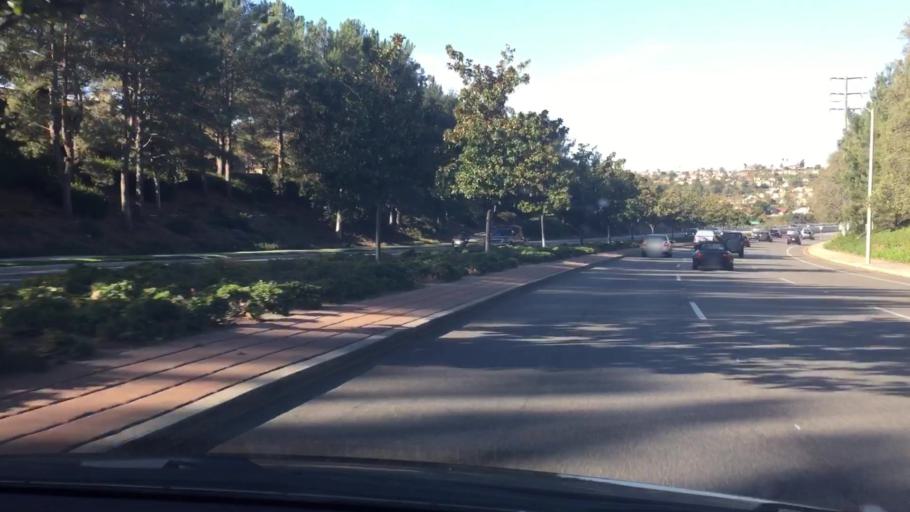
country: US
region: California
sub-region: Orange County
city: Rancho Santa Margarita
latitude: 33.6375
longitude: -117.6113
